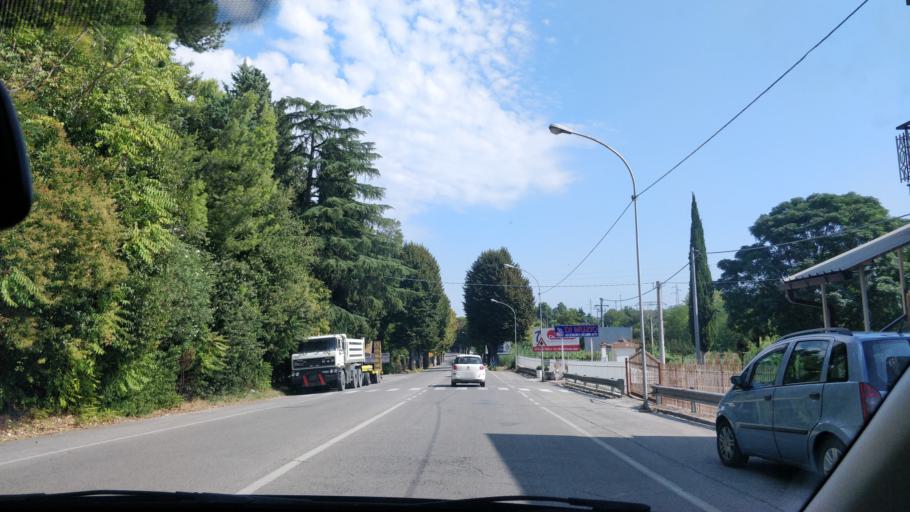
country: IT
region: Abruzzo
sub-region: Provincia di Chieti
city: Chieti
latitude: 42.3883
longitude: 14.1572
